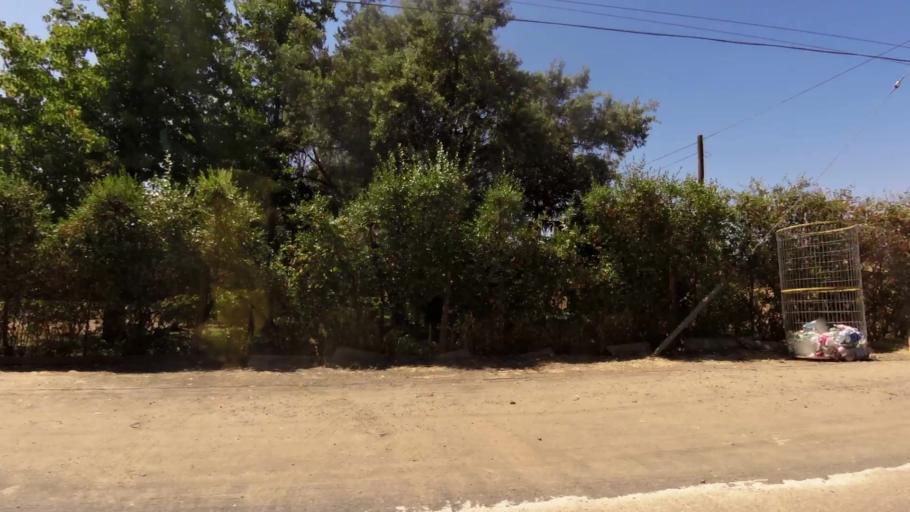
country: CL
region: Maule
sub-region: Provincia de Talca
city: Talca
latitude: -35.4244
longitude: -71.6149
